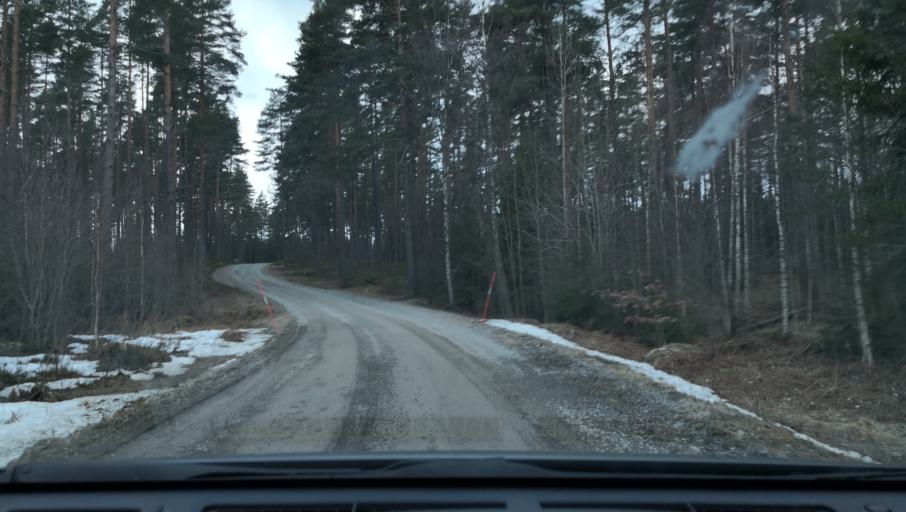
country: SE
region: Vaestmanland
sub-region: Kopings Kommun
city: Kolsva
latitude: 59.5584
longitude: 15.8646
